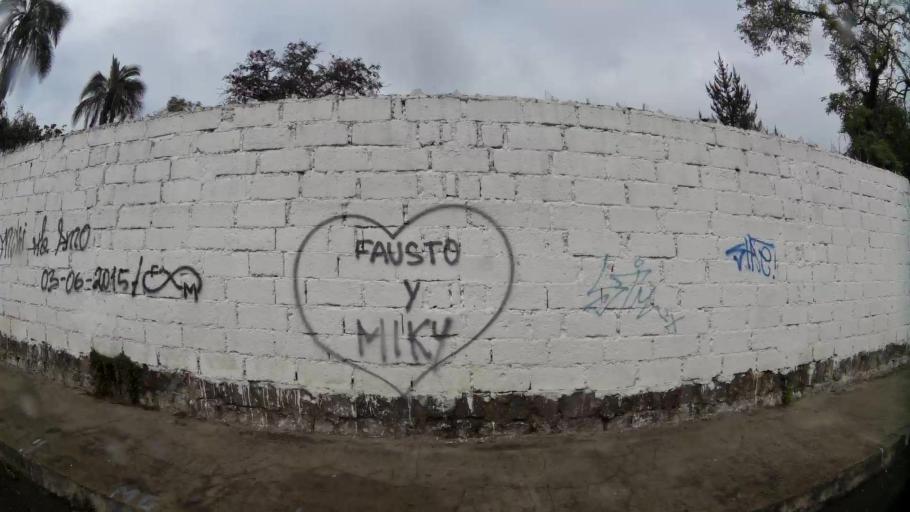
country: EC
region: Pichincha
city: Sangolqui
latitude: -0.2993
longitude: -78.4795
